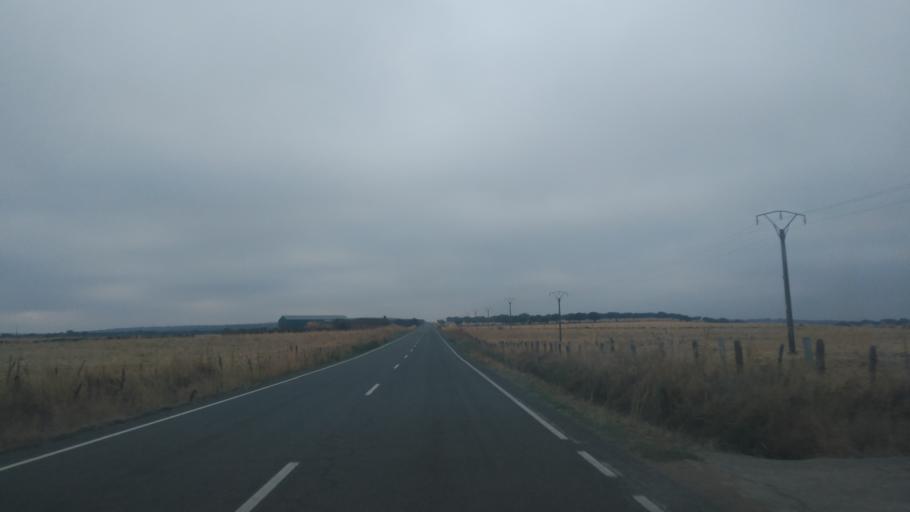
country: ES
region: Castille and Leon
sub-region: Provincia de Salamanca
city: Matilla de los Canos del Rio
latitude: 40.8197
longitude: -5.9399
